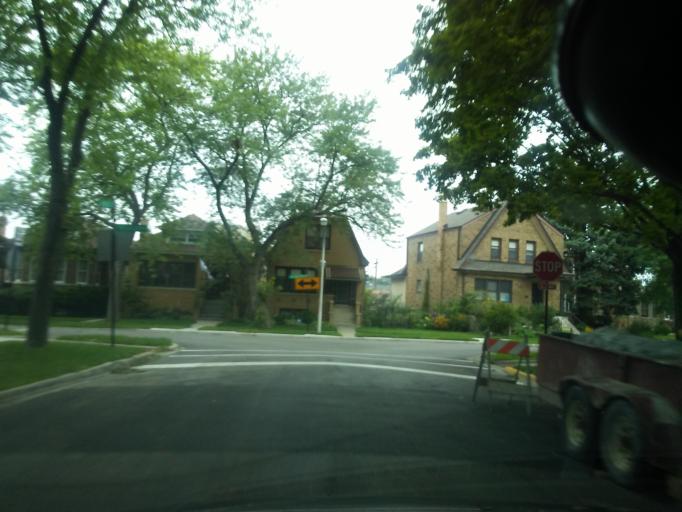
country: US
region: Illinois
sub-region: Cook County
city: Lincolnwood
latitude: 41.9718
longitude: -87.7404
